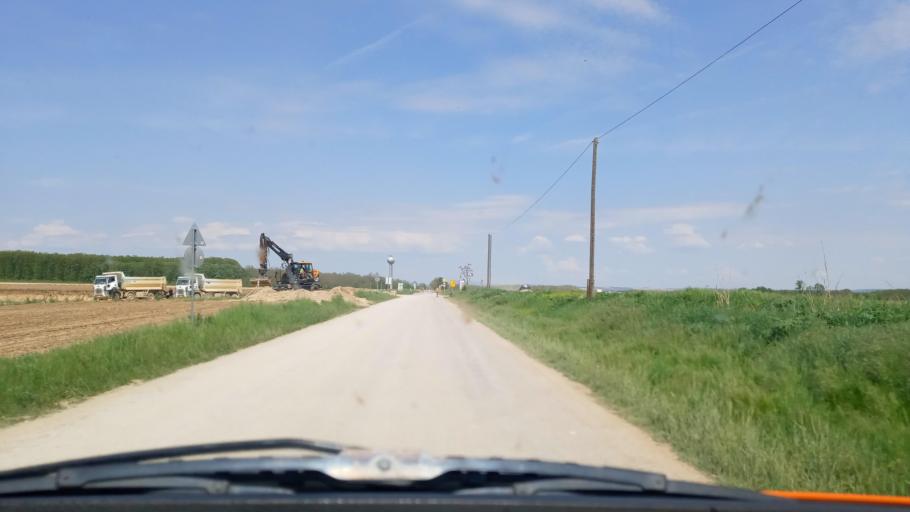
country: HU
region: Baranya
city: Boly
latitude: 45.8893
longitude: 18.5630
